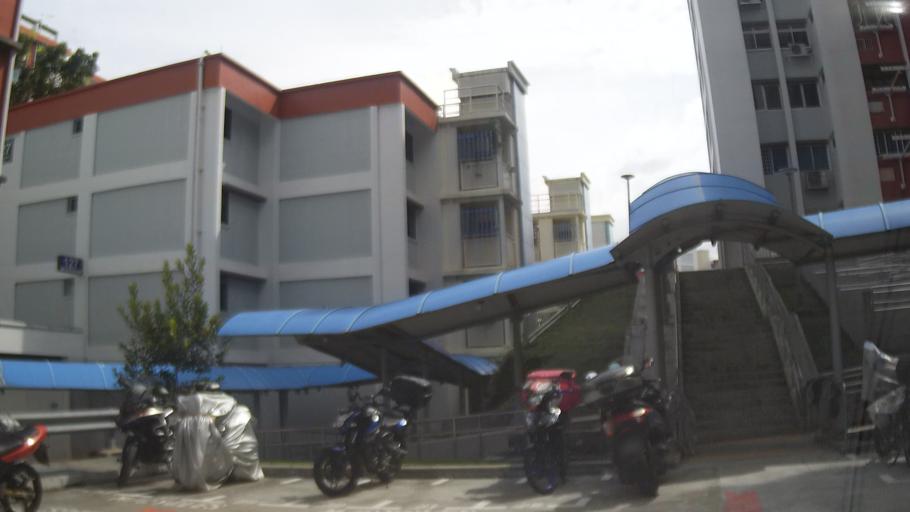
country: MY
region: Johor
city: Johor Bahru
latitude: 1.4380
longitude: 103.7791
